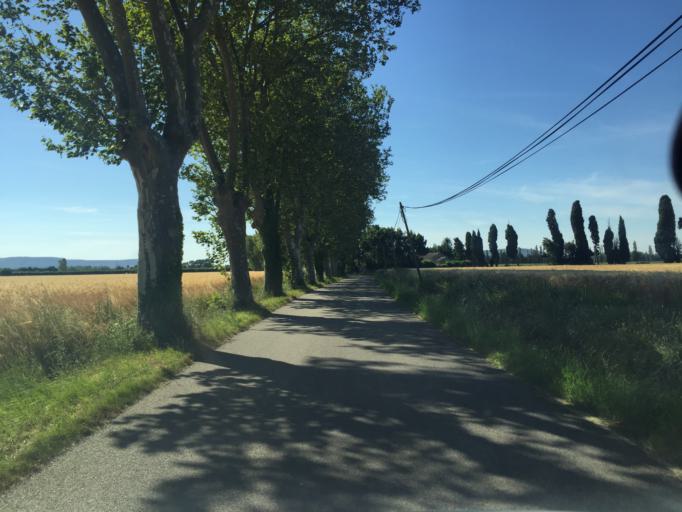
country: FR
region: Provence-Alpes-Cote d'Azur
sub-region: Departement du Vaucluse
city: Caderousse
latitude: 44.1066
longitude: 4.7498
